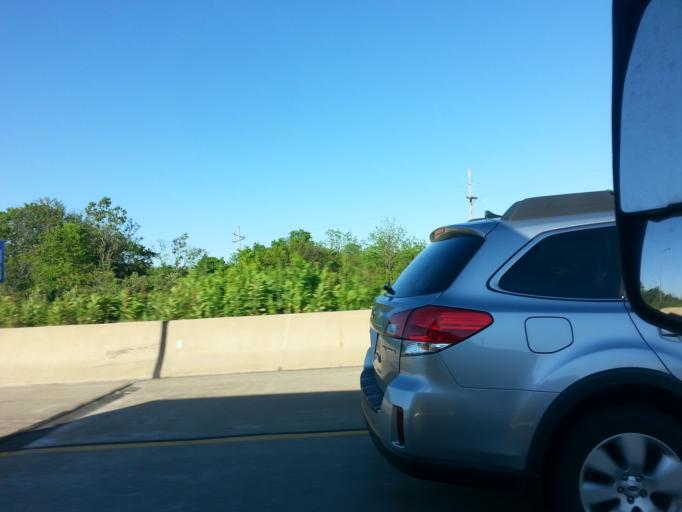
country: US
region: Illinois
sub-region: McLean County
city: Bloomington
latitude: 40.4529
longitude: -89.0243
